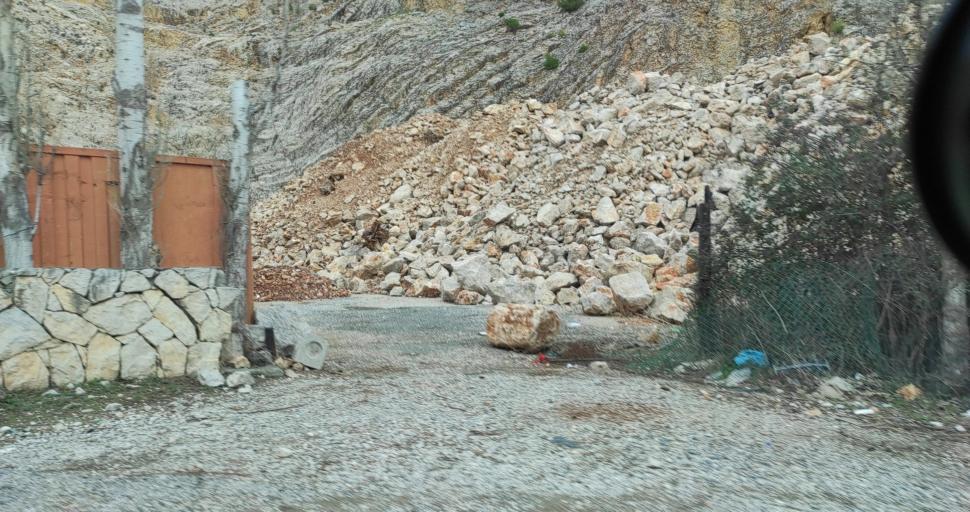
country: AL
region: Lezhe
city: Lezhe
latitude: 41.7893
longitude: 19.6265
